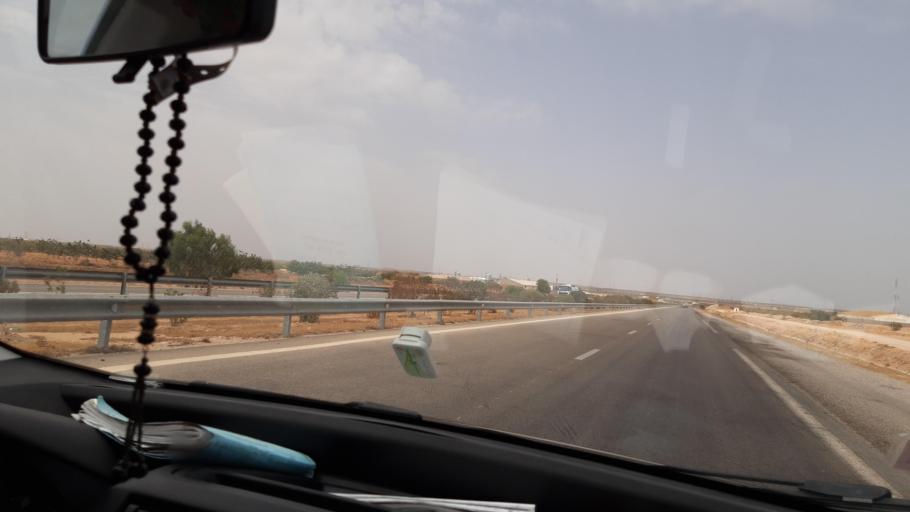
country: TN
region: Safaqis
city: Sfax
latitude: 34.8677
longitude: 10.6917
